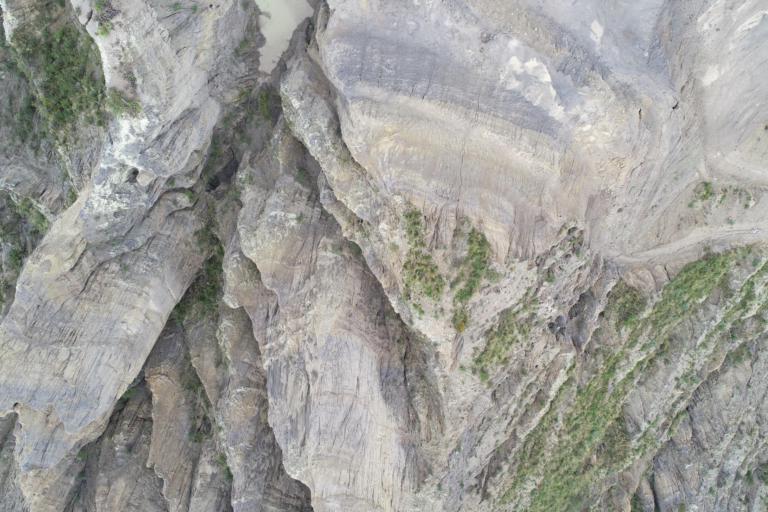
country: BO
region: La Paz
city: La Paz
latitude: -16.4990
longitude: -68.0782
